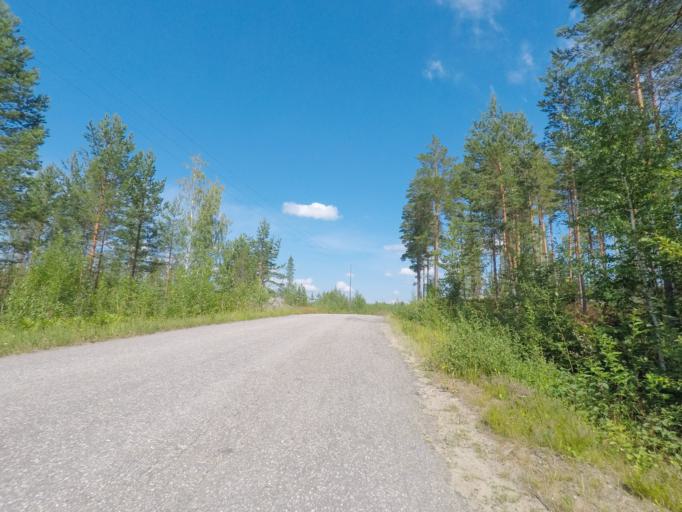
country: FI
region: Southern Savonia
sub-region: Mikkeli
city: Puumala
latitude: 61.4257
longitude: 28.1580
